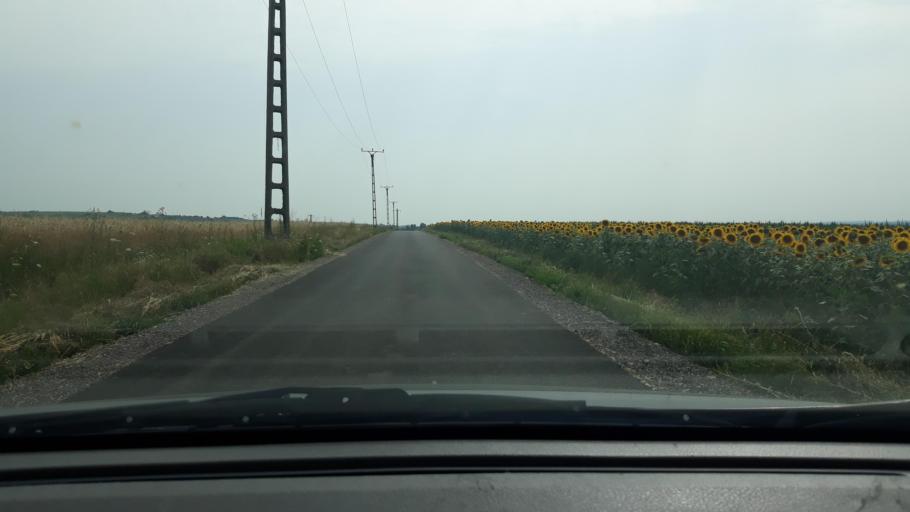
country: RO
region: Bihor
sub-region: Comuna Chislaz
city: Misca
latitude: 47.2741
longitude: 22.2709
